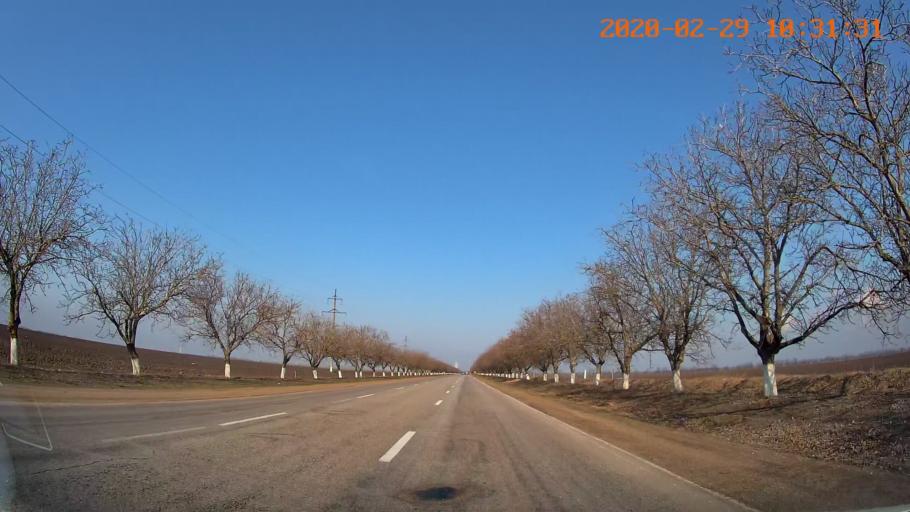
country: MD
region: Telenesti
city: Tiraspolul Nou
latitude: 46.9493
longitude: 29.5632
